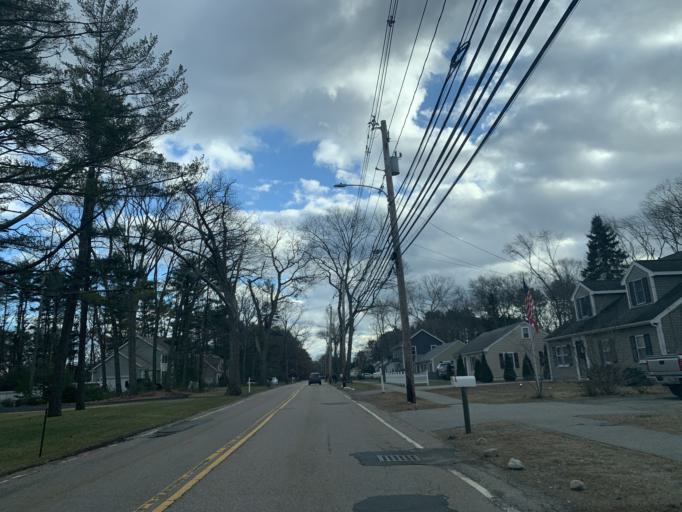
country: US
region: Massachusetts
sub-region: Norfolk County
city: Canton
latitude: 42.1804
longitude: -71.1446
